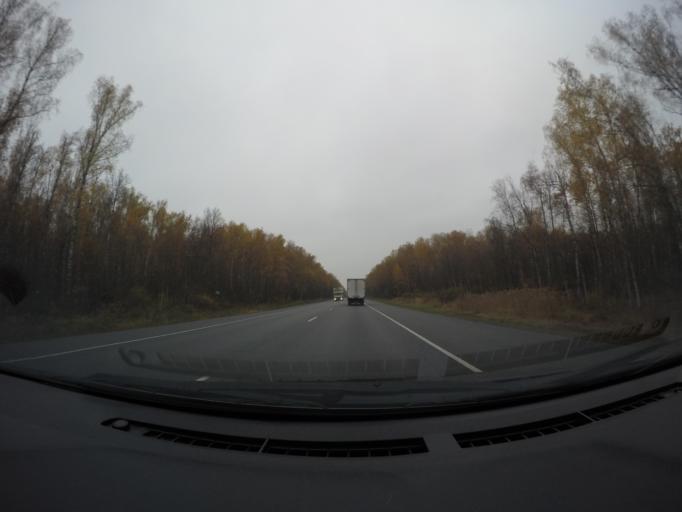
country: RU
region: Moskovskaya
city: Zhitnevo
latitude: 55.3636
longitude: 37.9469
